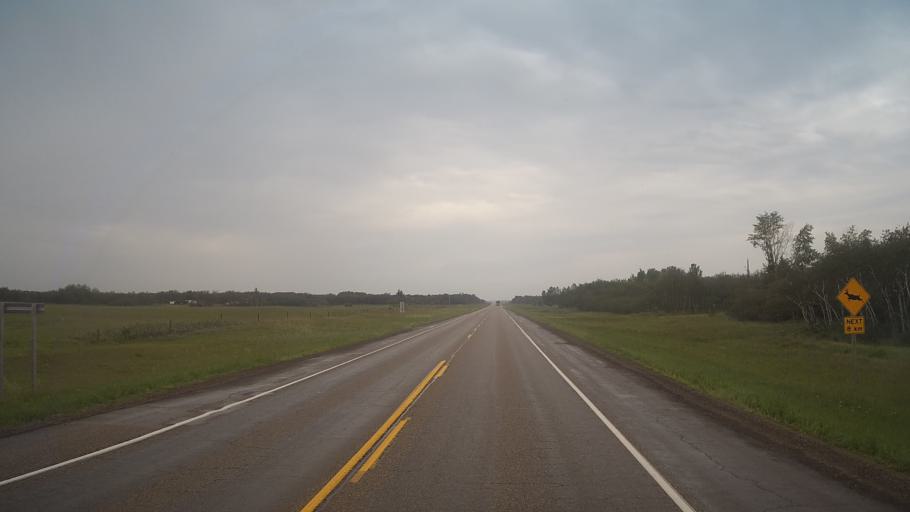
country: CA
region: Saskatchewan
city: Langham
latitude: 52.1293
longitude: -107.0299
